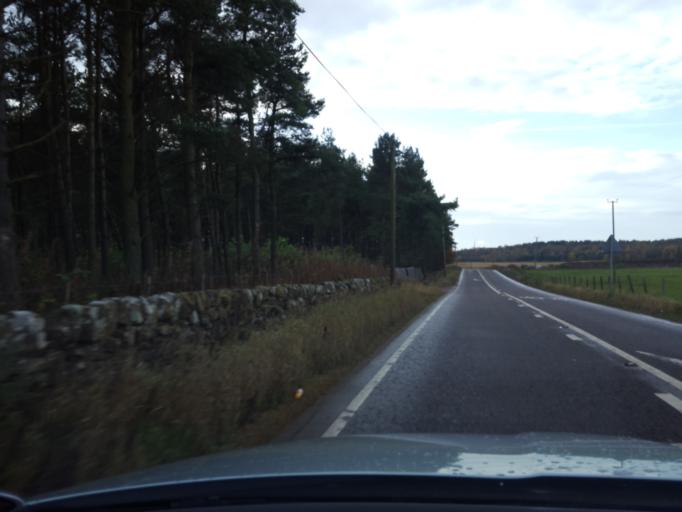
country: GB
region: Scotland
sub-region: South Lanarkshire
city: Carnwath
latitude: 55.7169
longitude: -3.5883
